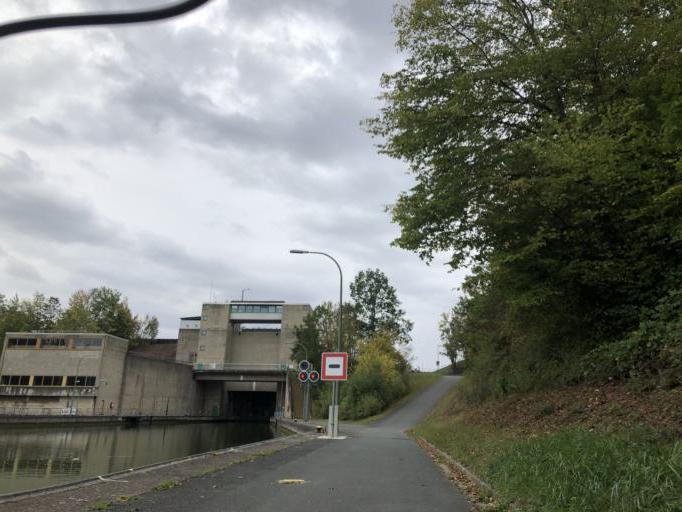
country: DE
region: Bavaria
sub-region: Regierungsbezirk Mittelfranken
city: Erlangen
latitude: 49.5576
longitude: 10.9695
